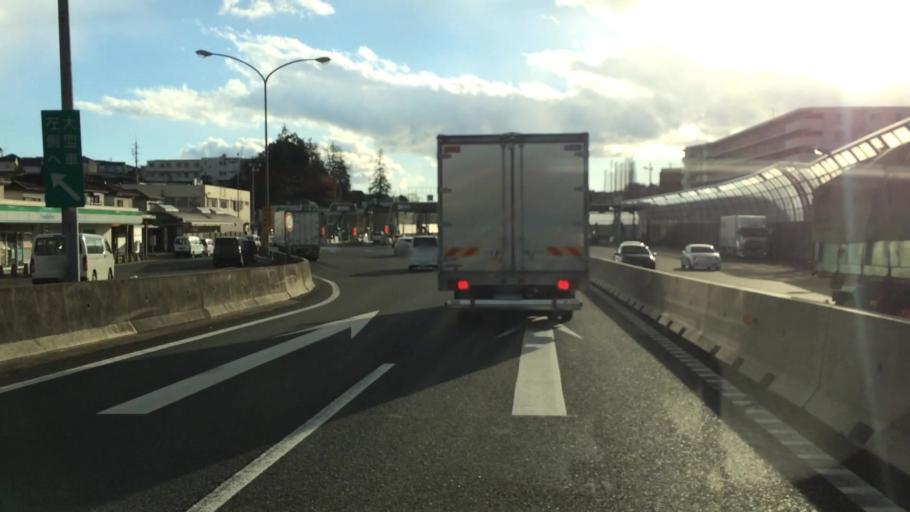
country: JP
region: Kanagawa
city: Yokohama
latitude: 35.4240
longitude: 139.5402
